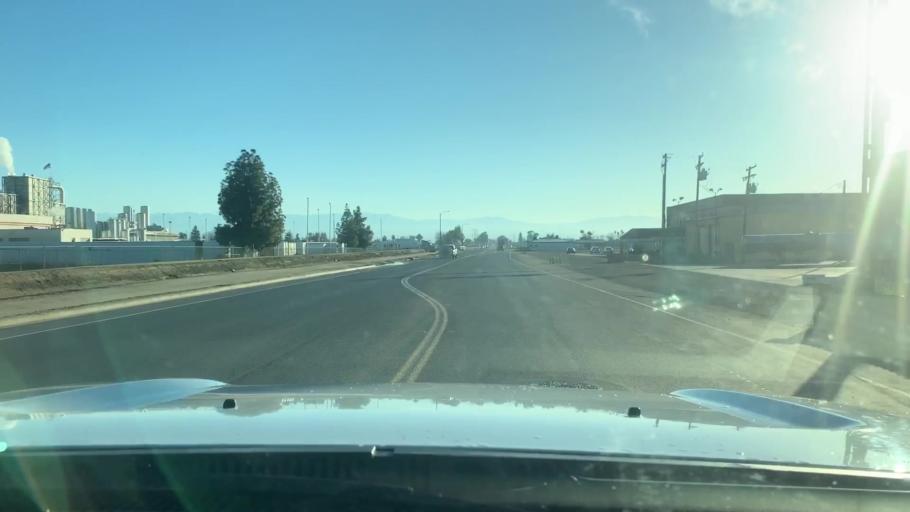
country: US
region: California
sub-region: Tulare County
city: Tulare
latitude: 36.1821
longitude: -119.3397
